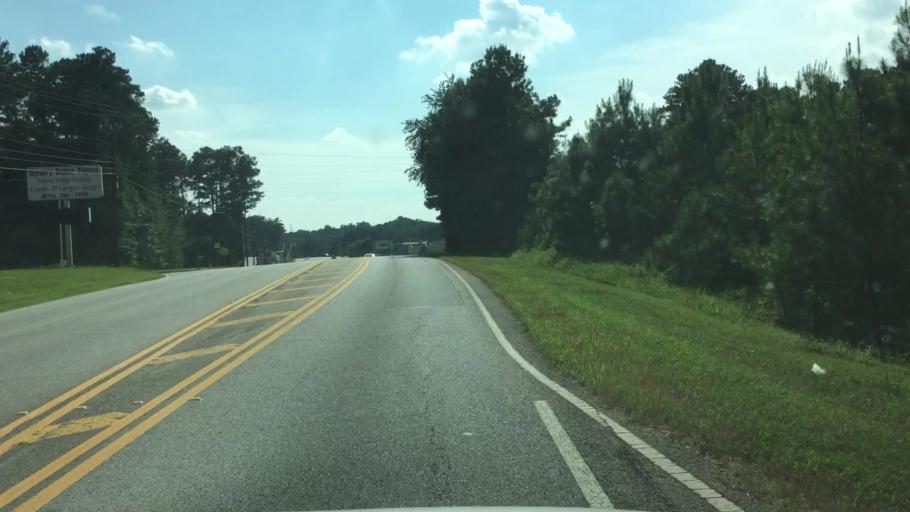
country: US
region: Georgia
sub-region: Barrow County
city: Auburn
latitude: 34.0110
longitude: -83.8471
